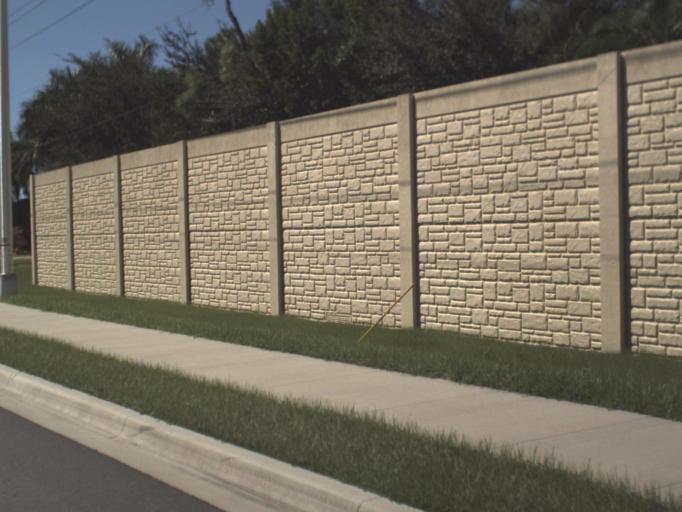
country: US
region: Florida
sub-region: Collier County
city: Lely
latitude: 26.1420
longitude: -81.7061
